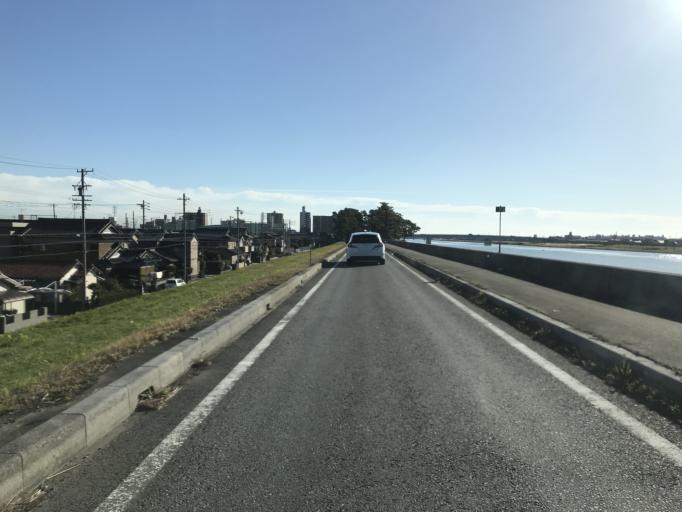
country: JP
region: Aichi
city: Kanie
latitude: 35.1302
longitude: 136.8389
